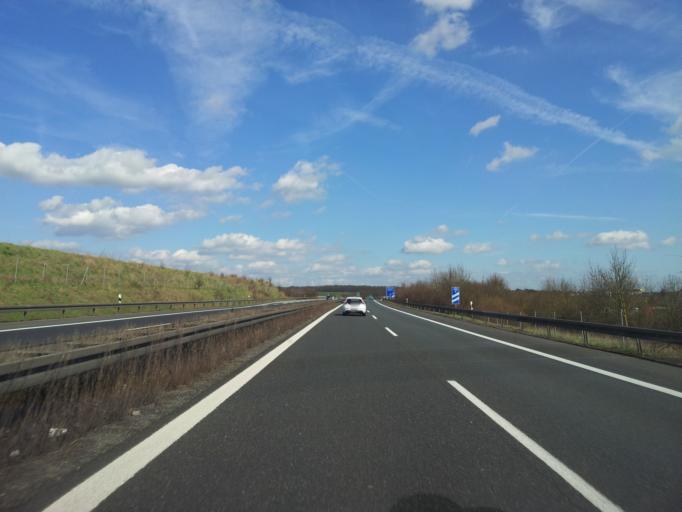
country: DE
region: Bavaria
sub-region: Regierungsbezirk Unterfranken
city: Sennfeld
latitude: 50.0292
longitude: 10.2600
